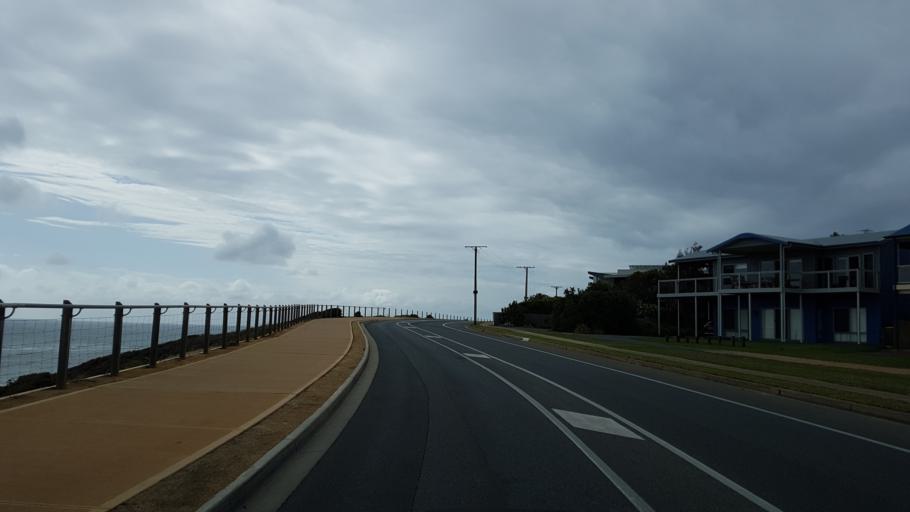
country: AU
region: South Australia
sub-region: Onkaparinga
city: Port Willunga
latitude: -35.2863
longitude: 138.4446
